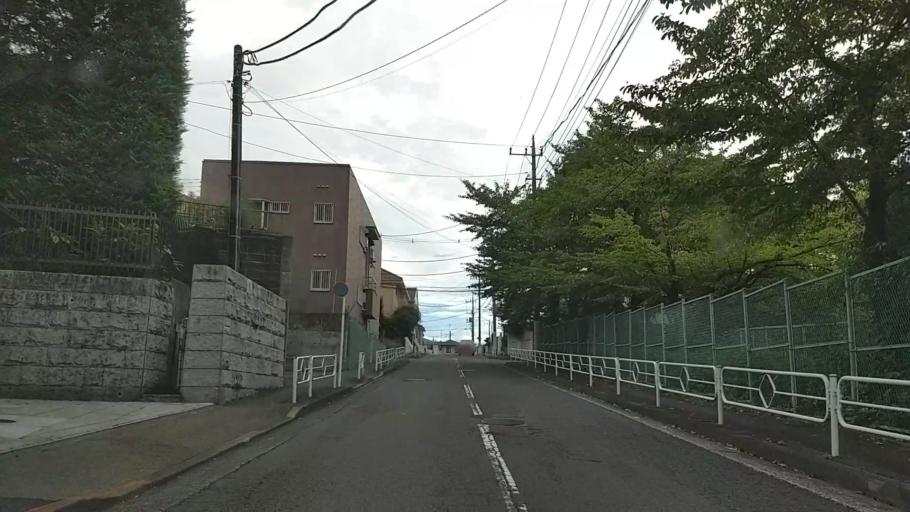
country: JP
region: Tokyo
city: Hachioji
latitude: 35.6389
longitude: 139.3156
